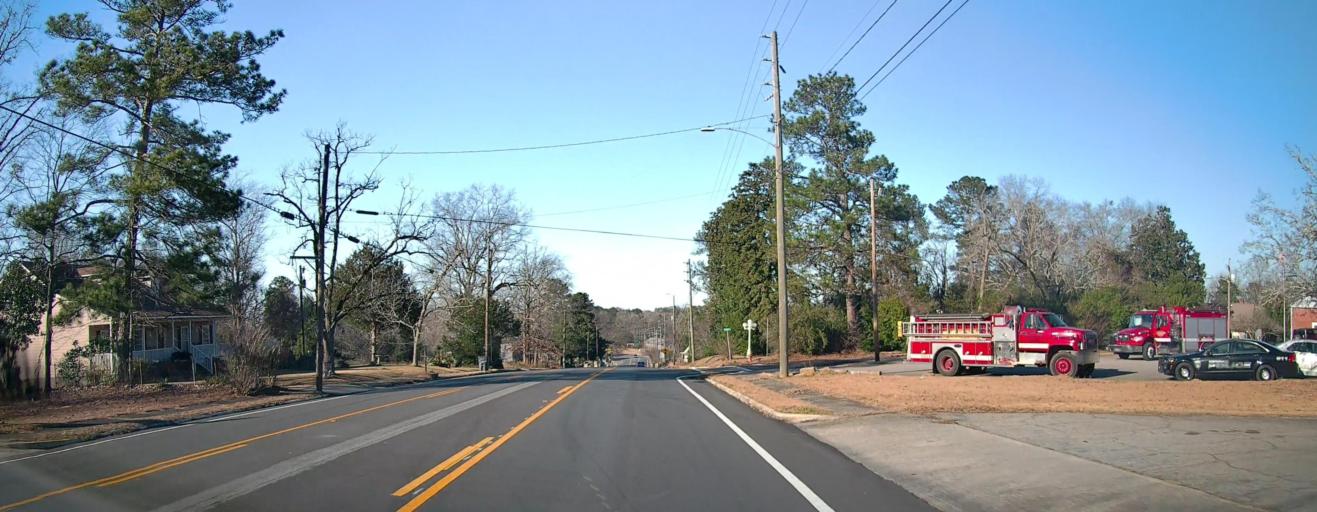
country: US
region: Georgia
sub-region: Meriwether County
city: Manchester
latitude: 32.8870
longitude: -84.6810
